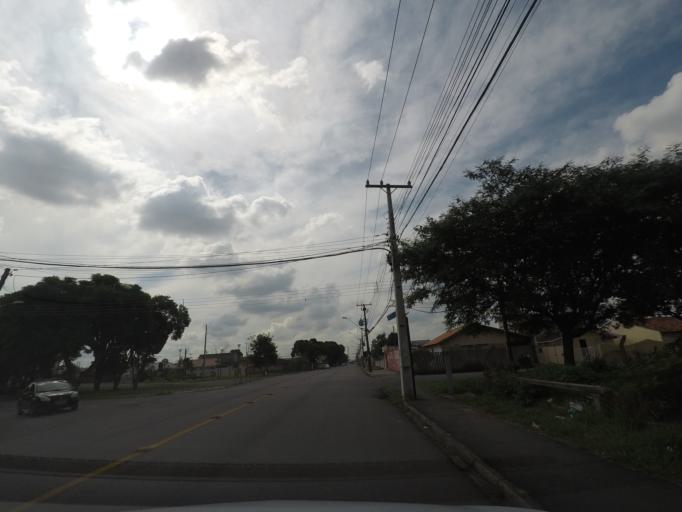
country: BR
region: Parana
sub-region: Pinhais
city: Pinhais
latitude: -25.4729
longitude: -49.2002
